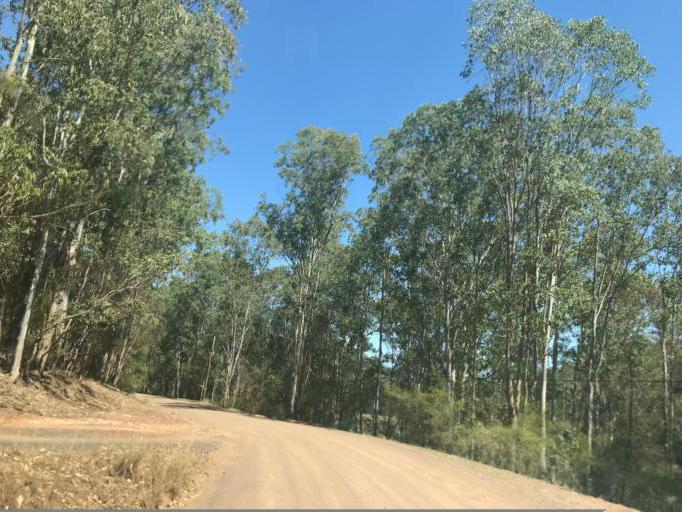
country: AU
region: New South Wales
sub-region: Hornsby Shire
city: Glenorie
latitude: -33.2557
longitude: 150.9755
